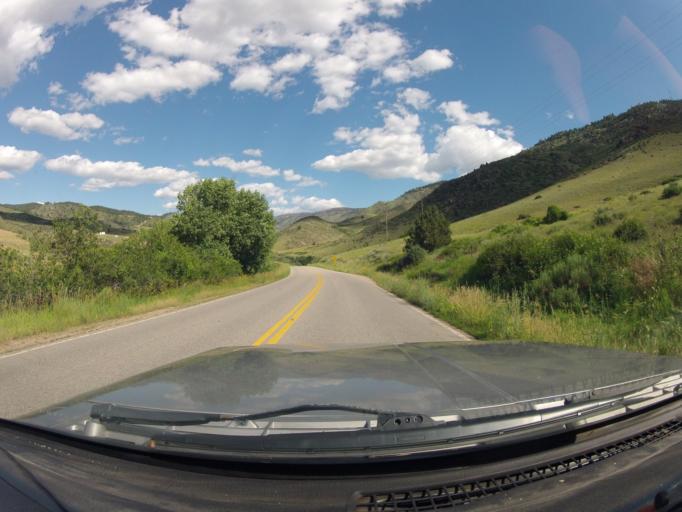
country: US
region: Colorado
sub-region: Larimer County
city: Laporte
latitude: 40.5343
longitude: -105.2715
